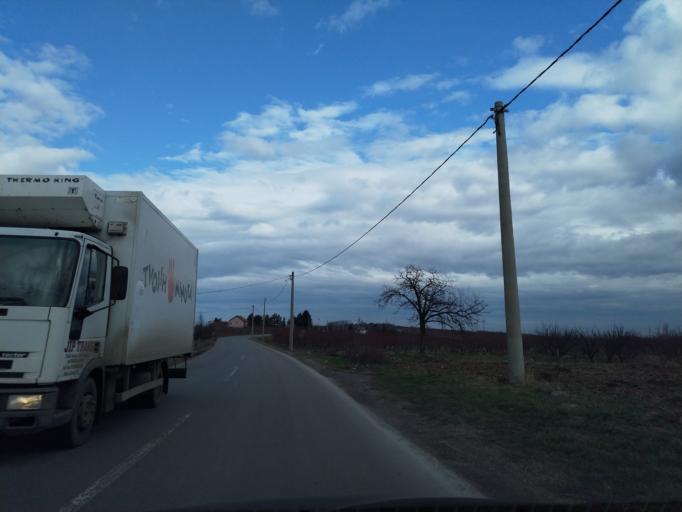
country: RS
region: Central Serbia
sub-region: Belgrade
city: Grocka
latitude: 44.6242
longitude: 20.7430
